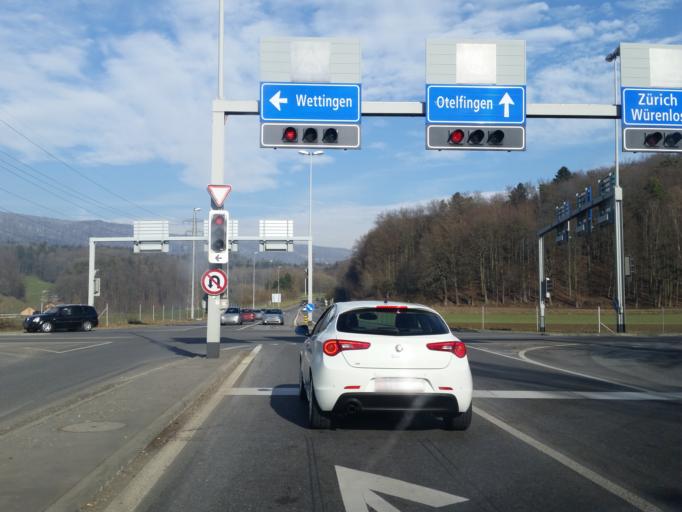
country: CH
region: Aargau
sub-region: Bezirk Baden
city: Wurenlos
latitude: 47.4538
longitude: 8.3487
